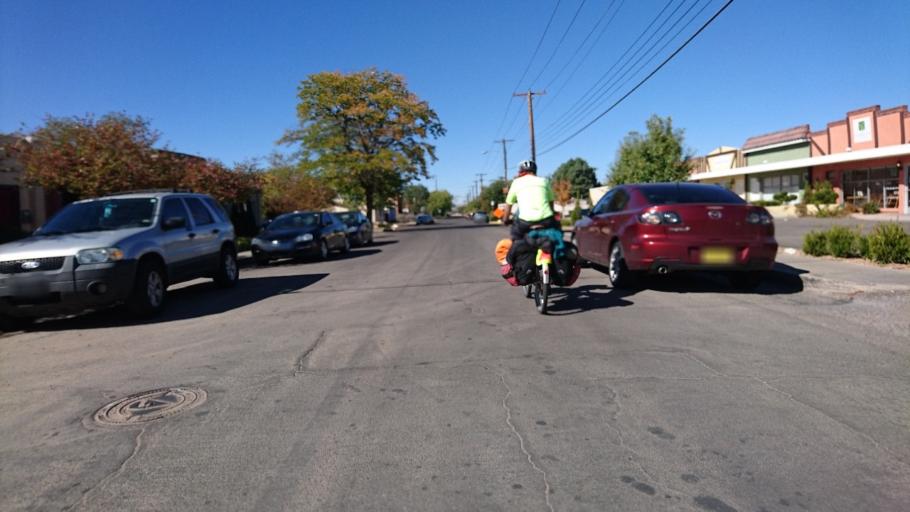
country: US
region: New Mexico
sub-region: Bernalillo County
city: Albuquerque
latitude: 35.0791
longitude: -106.6088
